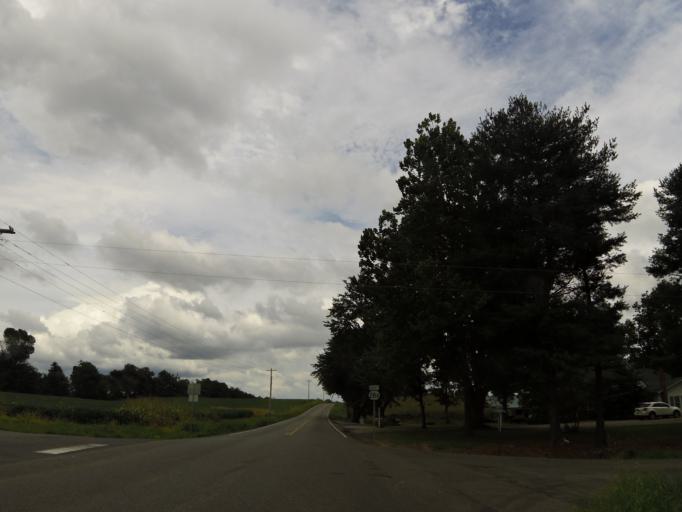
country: US
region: Kentucky
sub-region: Ballard County
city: La Center
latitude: 36.9903
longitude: -88.9348
